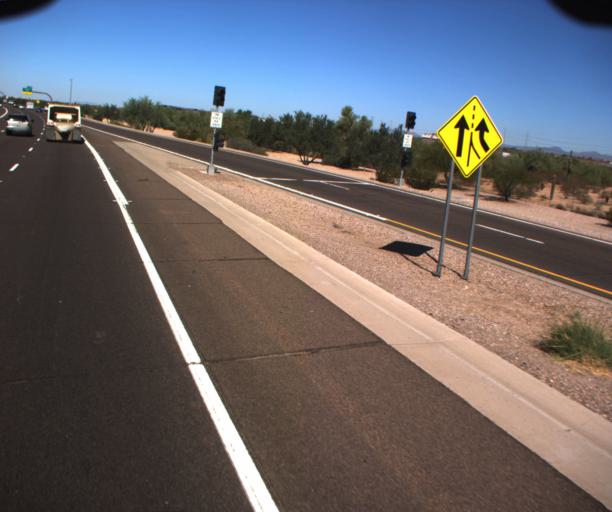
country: US
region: Arizona
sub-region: Maricopa County
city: Paradise Valley
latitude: 33.6492
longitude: -111.8950
